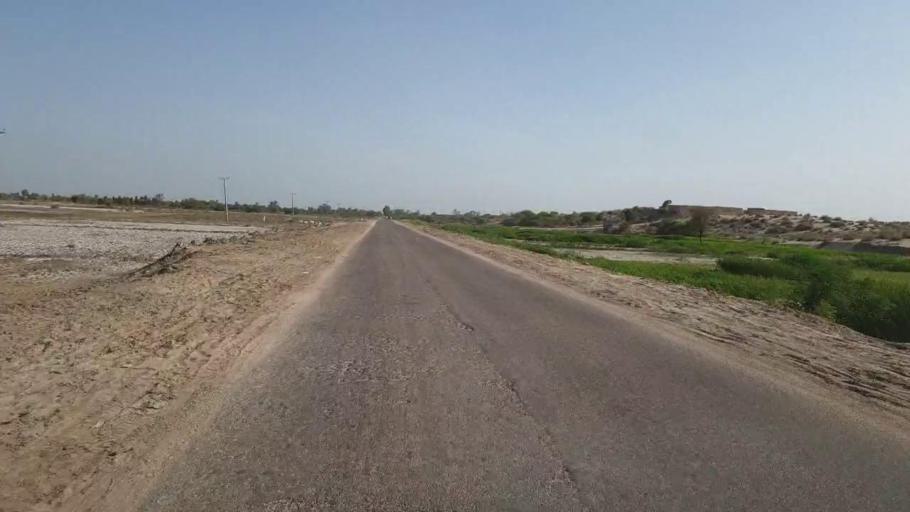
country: PK
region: Sindh
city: Daur
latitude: 26.4707
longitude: 68.4534
